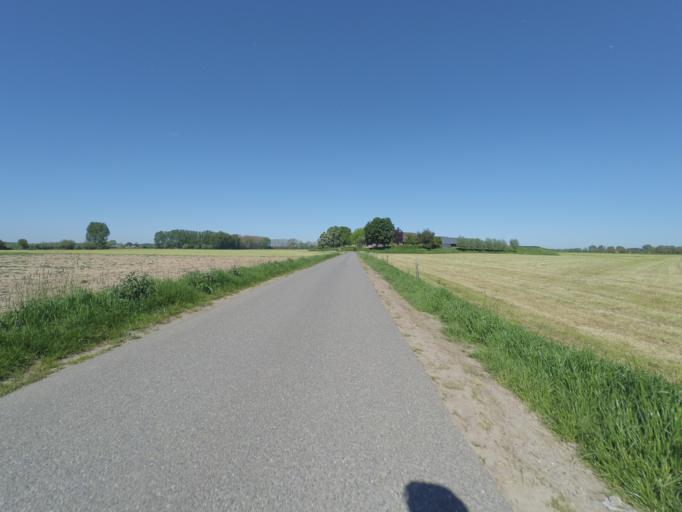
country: NL
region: Gelderland
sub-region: Gemeente Lochem
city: Epse
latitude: 52.2135
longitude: 6.1801
